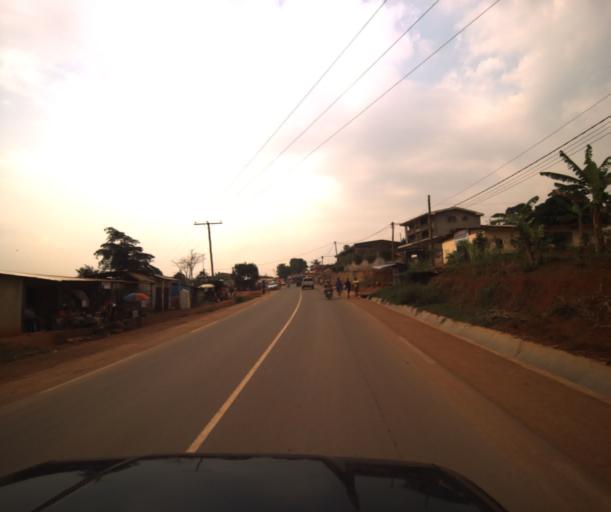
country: CM
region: Centre
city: Yaounde
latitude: 3.8181
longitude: 11.4710
